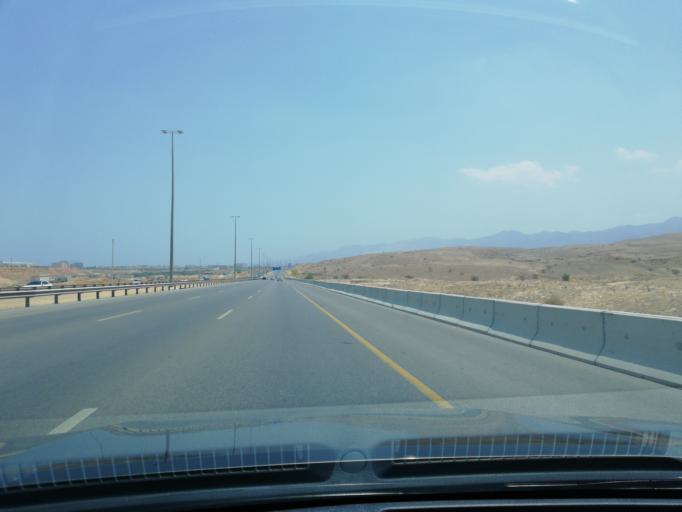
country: OM
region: Muhafazat Masqat
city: Bawshar
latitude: 23.5567
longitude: 58.3119
